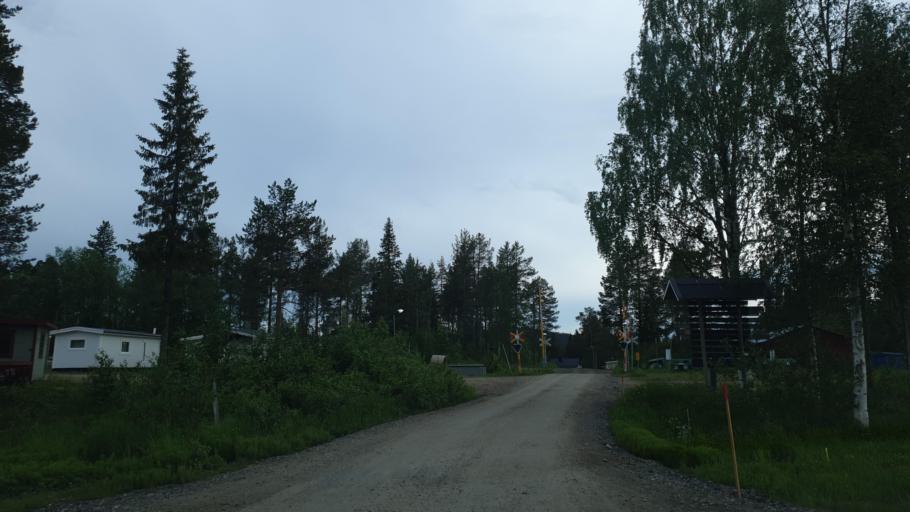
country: SE
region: Norrbotten
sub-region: Jokkmokks Kommun
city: Jokkmokk
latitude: 66.1556
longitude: 19.9863
